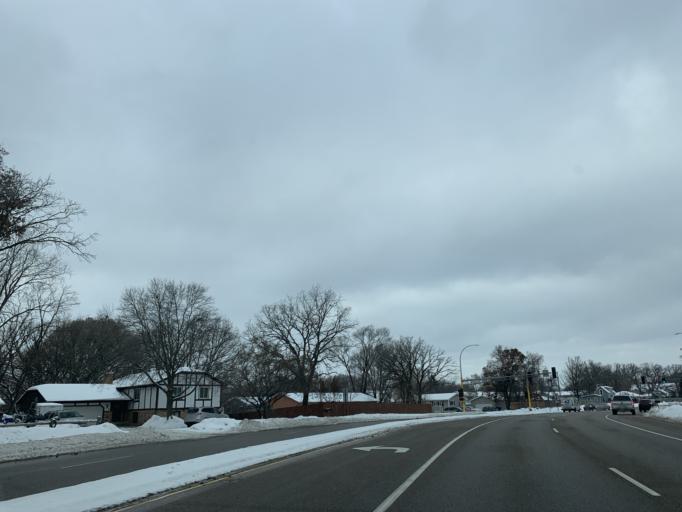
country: US
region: Minnesota
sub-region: Anoka County
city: Blaine
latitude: 45.1630
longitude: -93.2762
